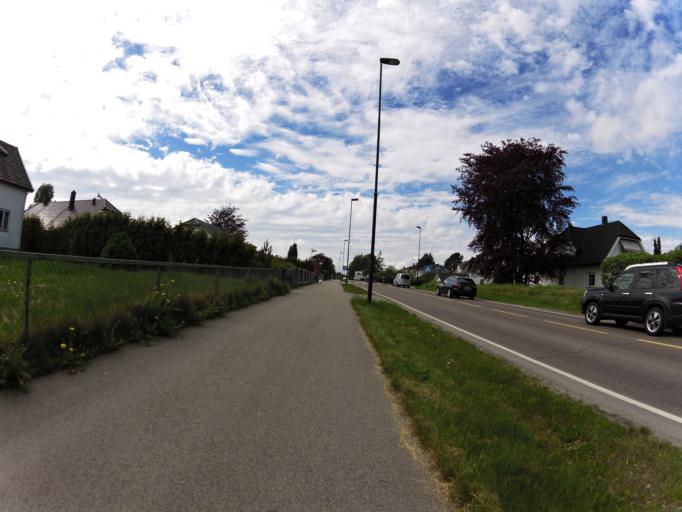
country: NO
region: Ostfold
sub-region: Rade
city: Karlshus
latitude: 59.3535
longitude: 10.8634
